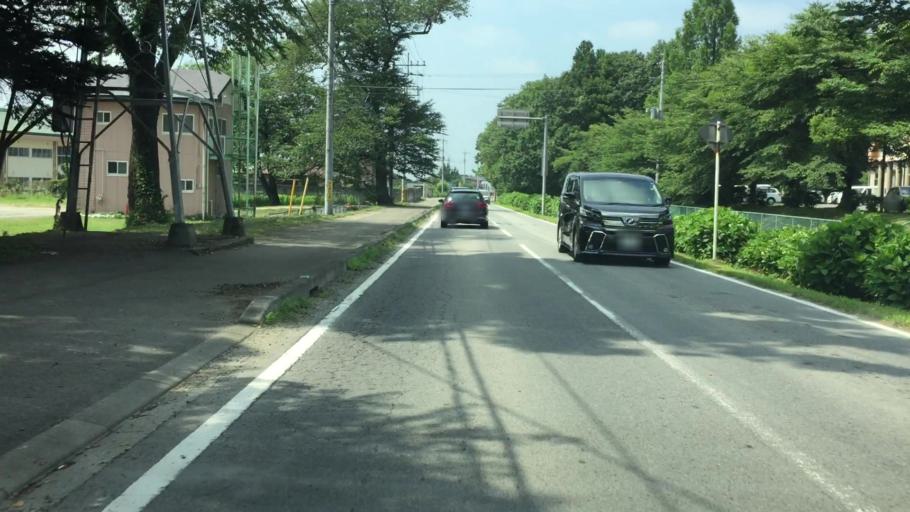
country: JP
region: Tochigi
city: Kuroiso
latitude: 36.9939
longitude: 139.9937
